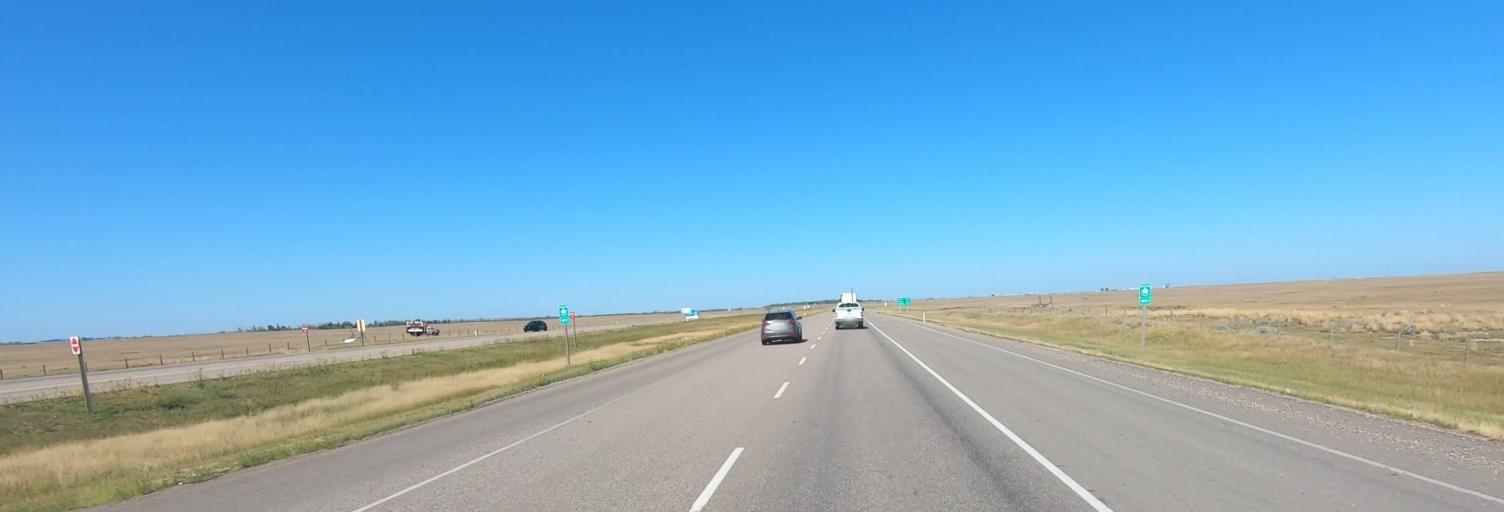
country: CA
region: Alberta
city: Brooks
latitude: 50.5225
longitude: -111.7594
